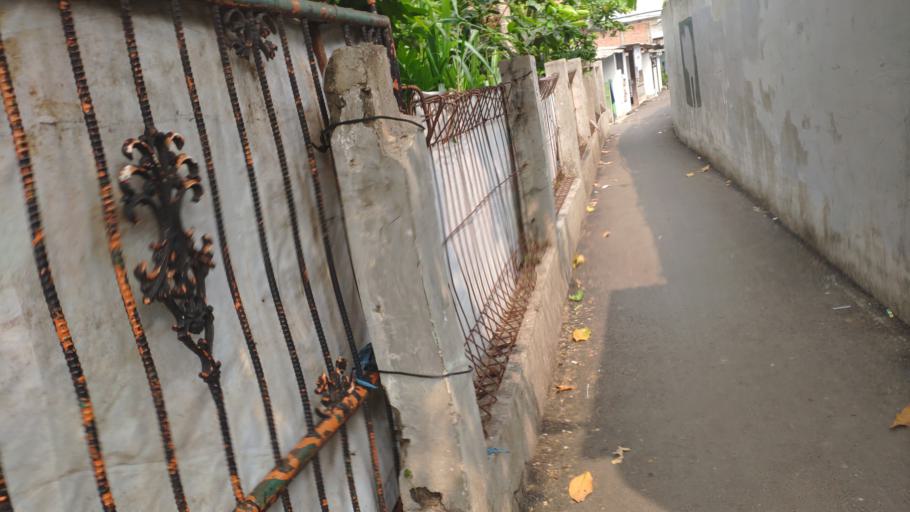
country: ID
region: West Java
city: Depok
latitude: -6.3459
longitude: 106.8143
